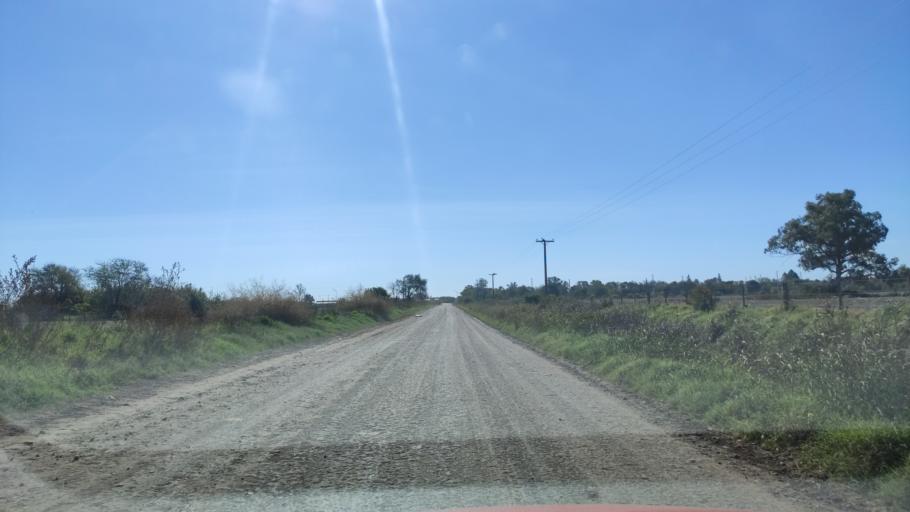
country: AR
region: Cordoba
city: Leones
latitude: -32.6671
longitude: -62.3120
